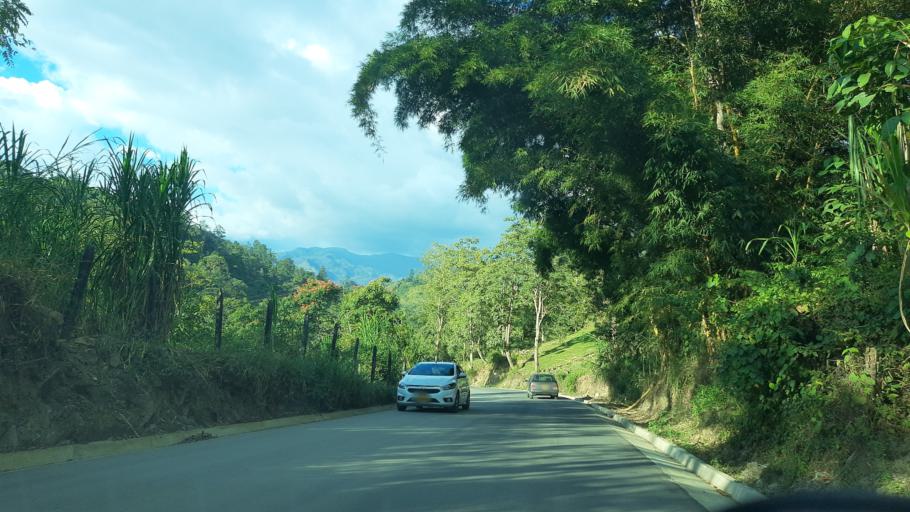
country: CO
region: Boyaca
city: Garagoa
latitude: 5.0849
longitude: -73.3826
